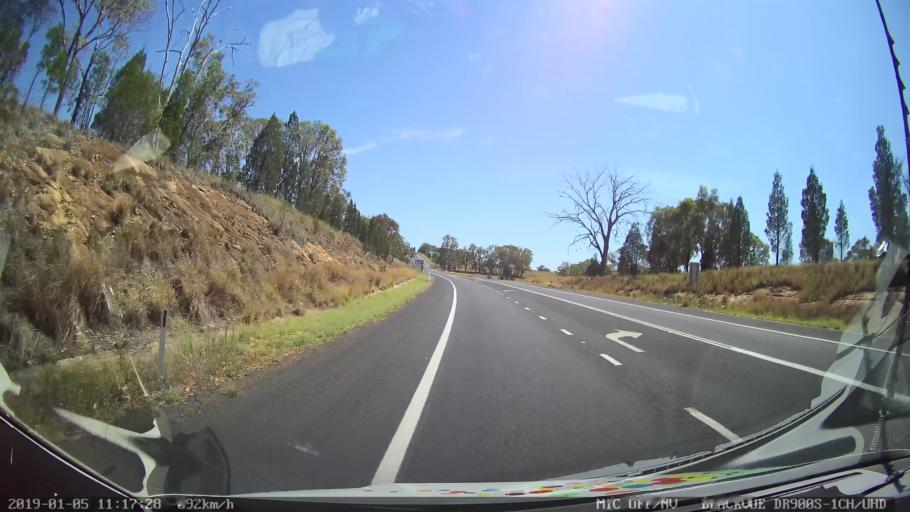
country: AU
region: New South Wales
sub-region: Warrumbungle Shire
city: Coonabarabran
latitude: -31.3263
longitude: 149.3074
